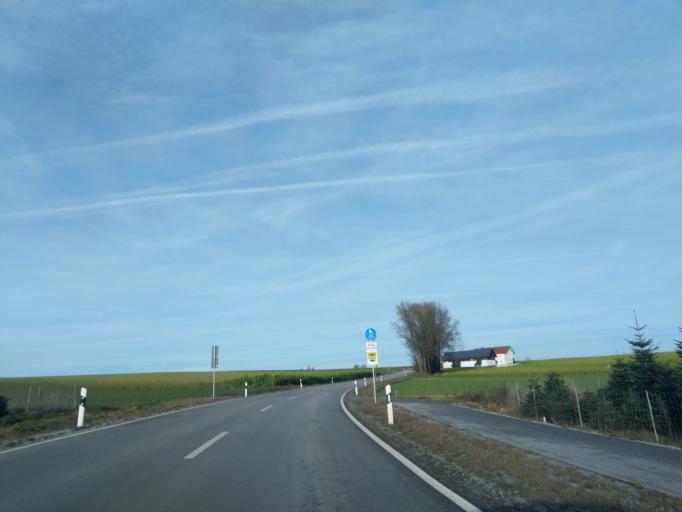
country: DE
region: Bavaria
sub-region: Lower Bavaria
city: Wallerfing
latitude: 48.6667
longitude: 12.8698
